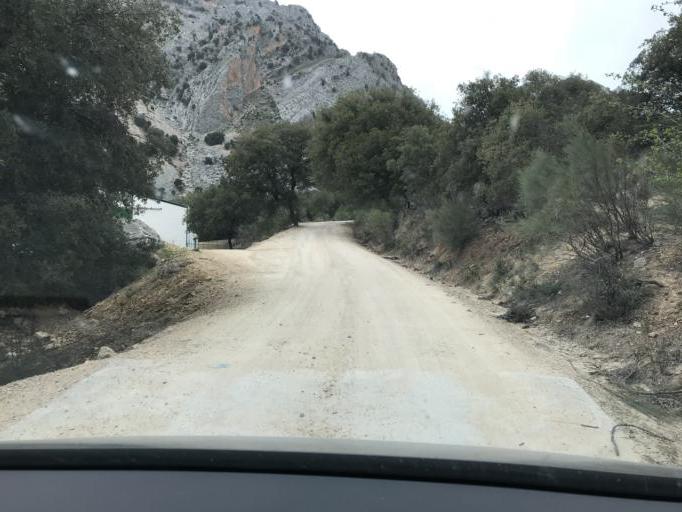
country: ES
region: Andalusia
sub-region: Provincia de Granada
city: Castril
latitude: 37.8862
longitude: -2.7517
